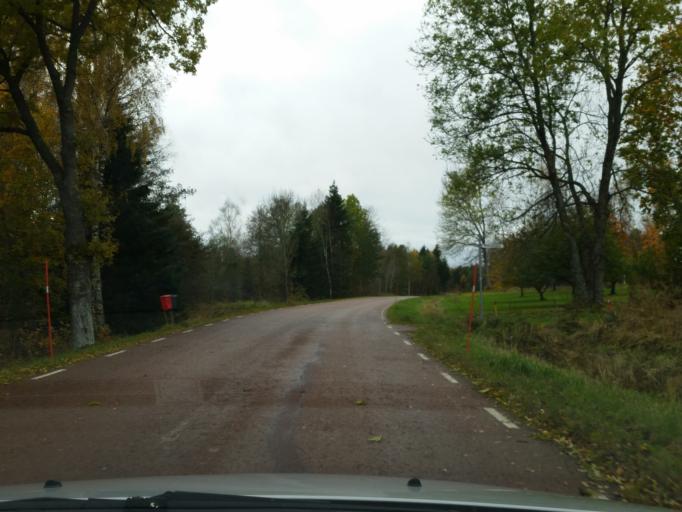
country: AX
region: Alands landsbygd
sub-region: Lemland
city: Lemland
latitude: 60.0231
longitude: 20.1572
